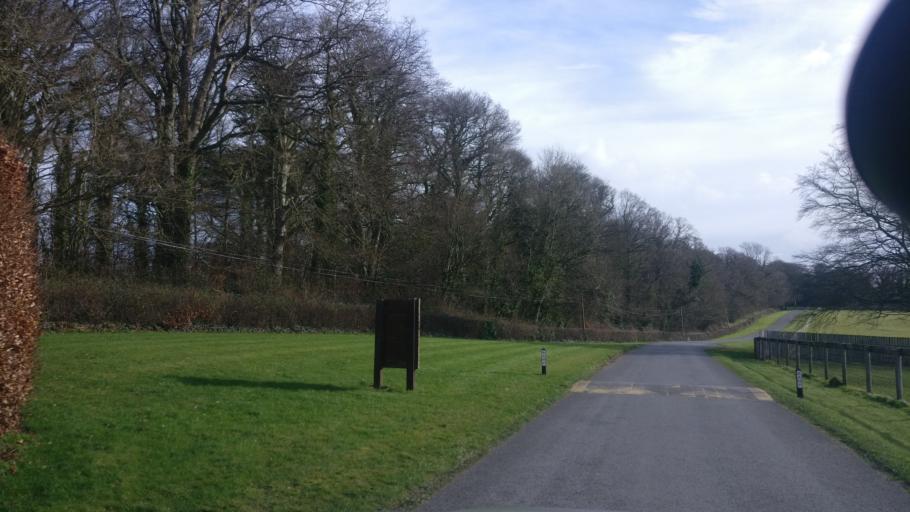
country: IE
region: Leinster
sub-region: Kilkenny
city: Thomastown
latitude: 52.5315
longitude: -7.1730
